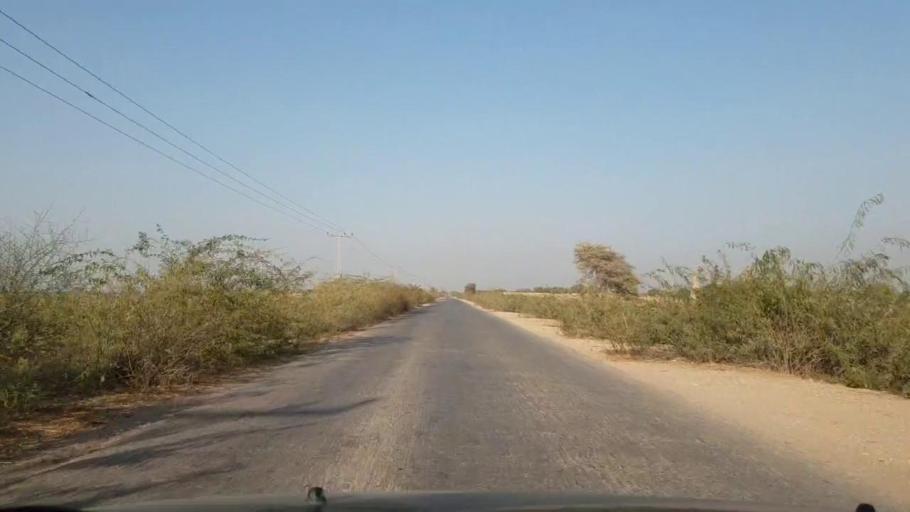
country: PK
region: Sindh
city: Chambar
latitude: 25.2504
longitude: 68.7917
